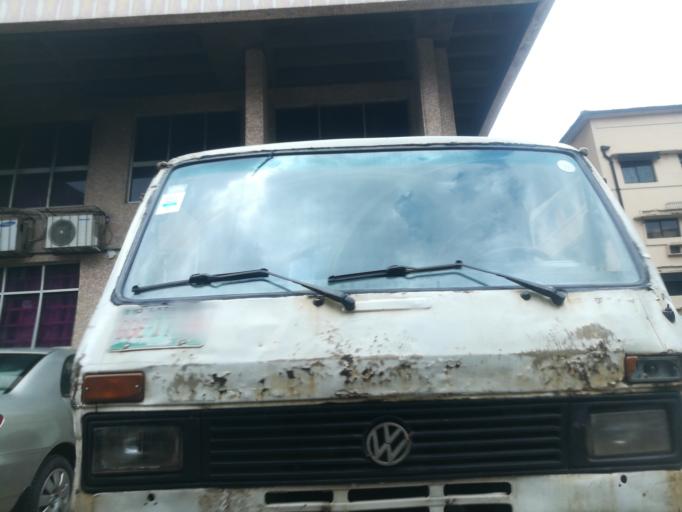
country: NG
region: Lagos
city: Lagos
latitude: 6.4581
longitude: 3.3811
